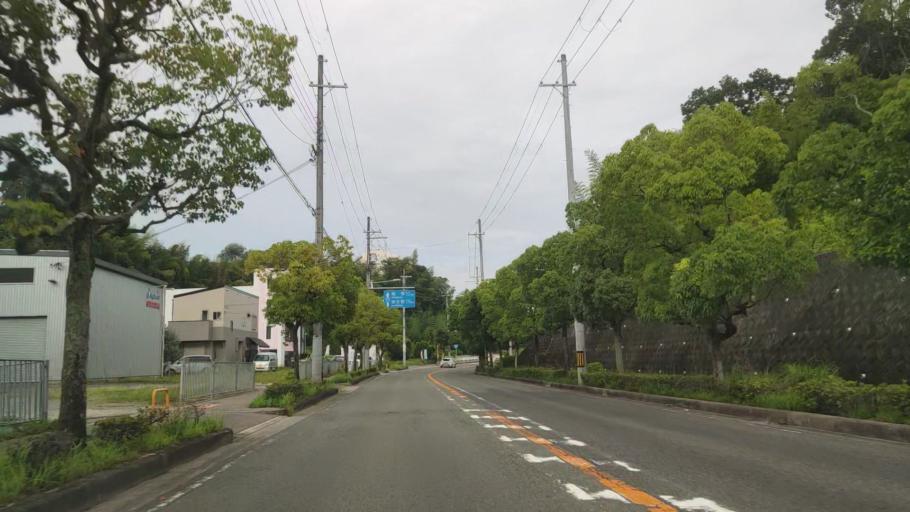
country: JP
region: Osaka
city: Tondabayashicho
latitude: 34.4251
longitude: 135.5732
